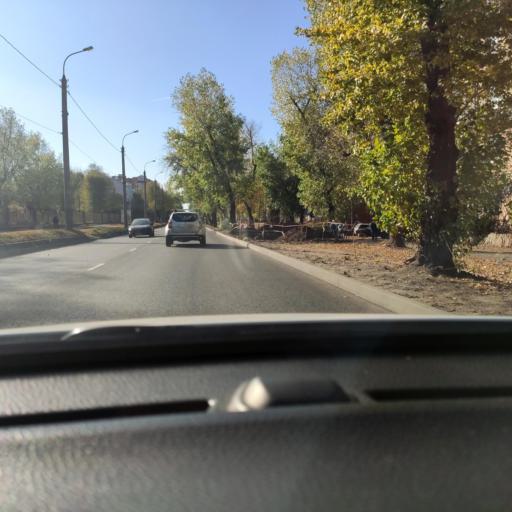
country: RU
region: Voronezj
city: Voronezh
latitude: 51.6418
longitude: 39.2407
